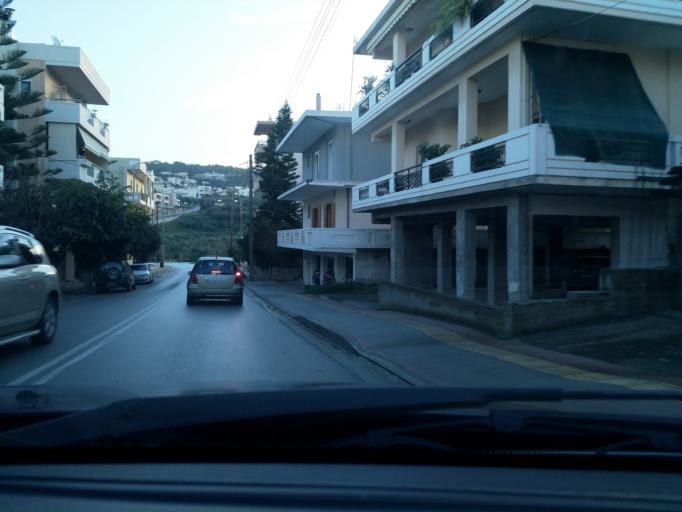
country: GR
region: Crete
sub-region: Nomos Chanias
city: Chania
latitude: 35.5118
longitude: 24.0436
